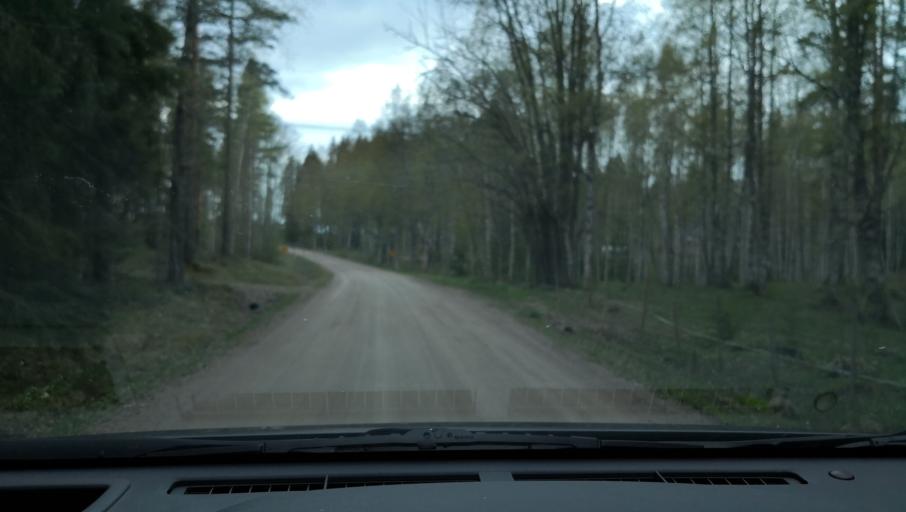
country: SE
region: Vaestmanland
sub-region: Fagersta Kommun
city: Fagersta
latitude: 60.1197
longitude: 15.7908
